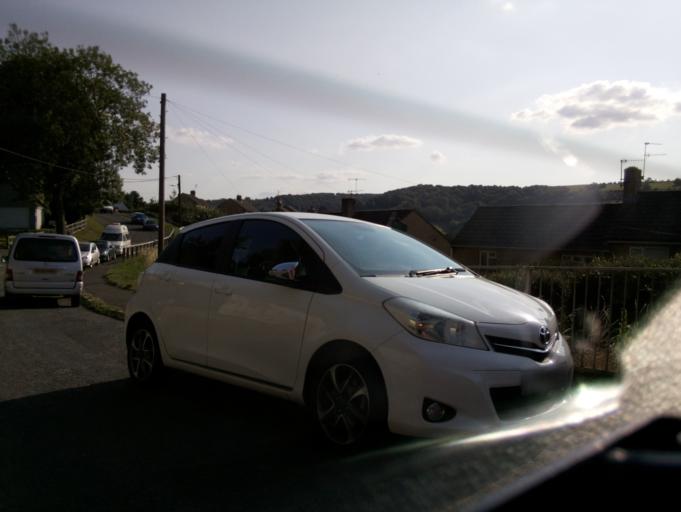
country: GB
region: England
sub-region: Gloucestershire
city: Stroud
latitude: 51.7312
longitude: -2.2278
